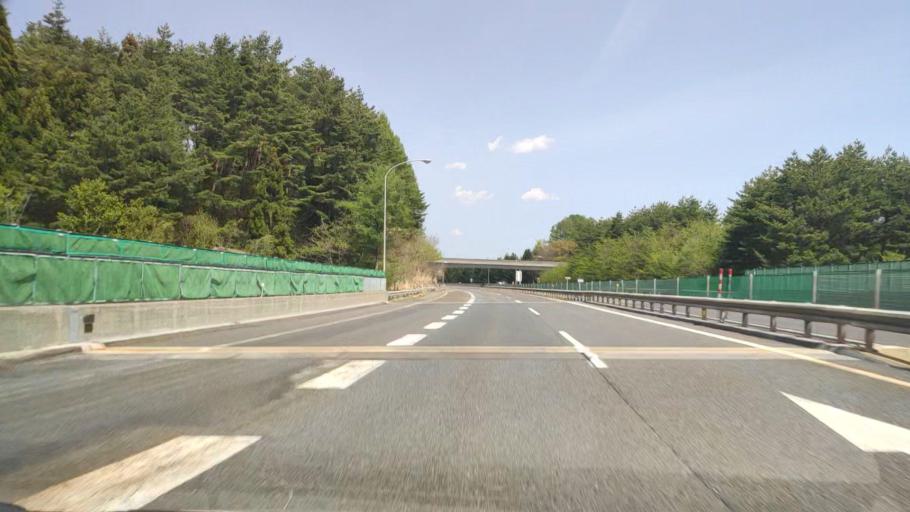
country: JP
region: Iwate
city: Ichinohe
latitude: 40.2528
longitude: 141.4026
